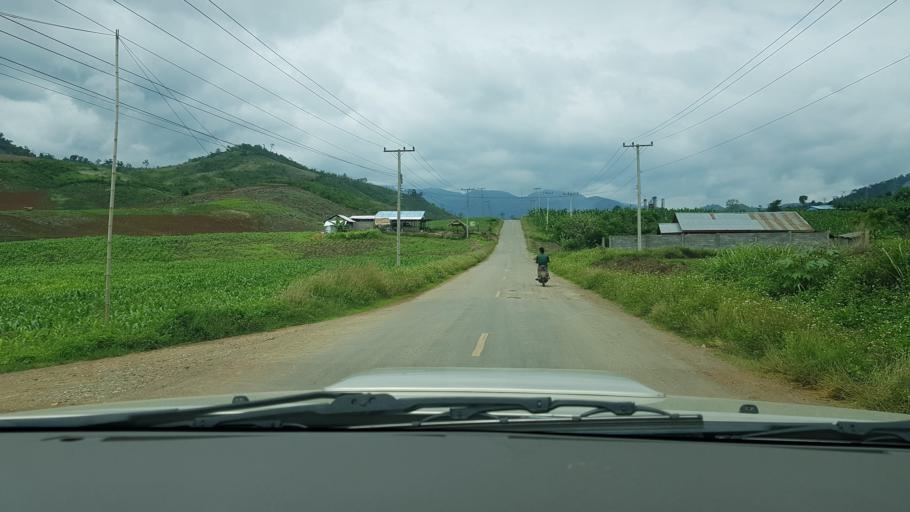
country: TH
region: Nan
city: Chaloem Phra Kiat
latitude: 19.9837
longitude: 101.2753
